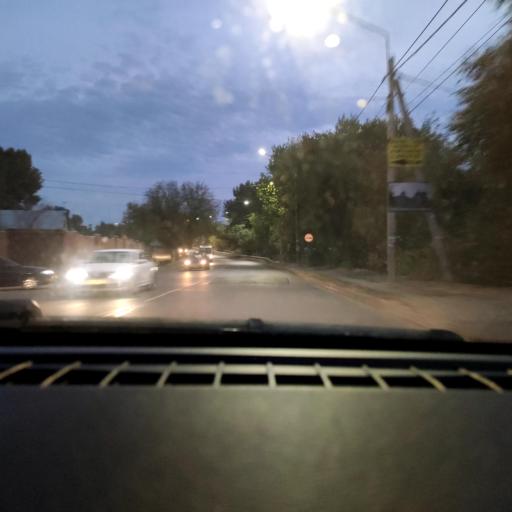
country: RU
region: Voronezj
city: Voronezh
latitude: 51.7293
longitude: 39.2599
